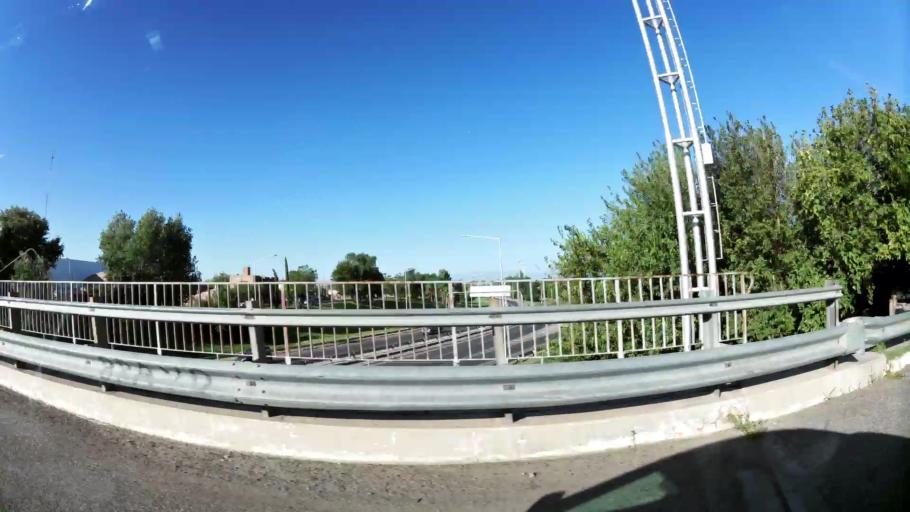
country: AR
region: San Juan
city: Villa Krause
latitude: -31.5552
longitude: -68.5175
